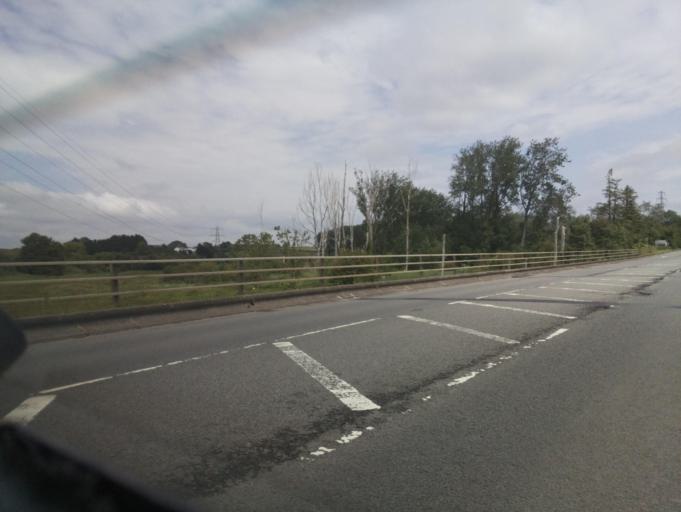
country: GB
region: Wales
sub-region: Vale of Glamorgan
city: Rhoose
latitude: 51.4008
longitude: -3.3911
